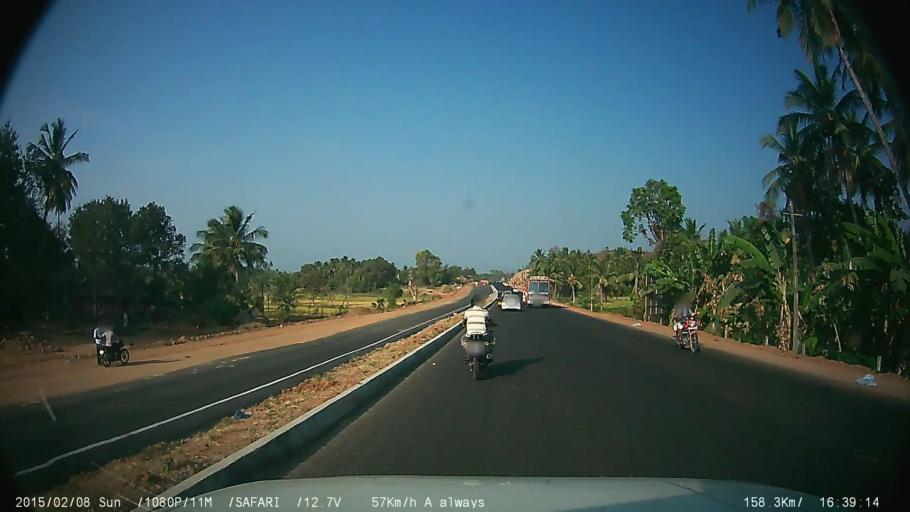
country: IN
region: Kerala
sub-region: Palakkad district
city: Palakkad
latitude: 10.6925
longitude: 76.5852
